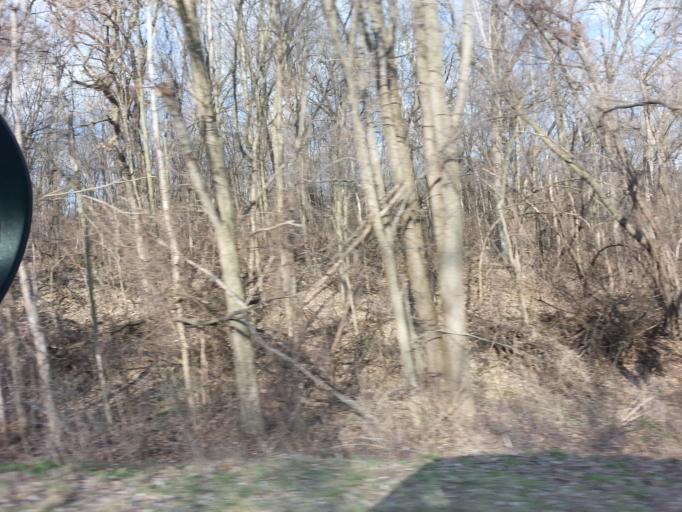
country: US
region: Minnesota
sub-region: Washington County
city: Afton
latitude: 44.8992
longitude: -92.8429
